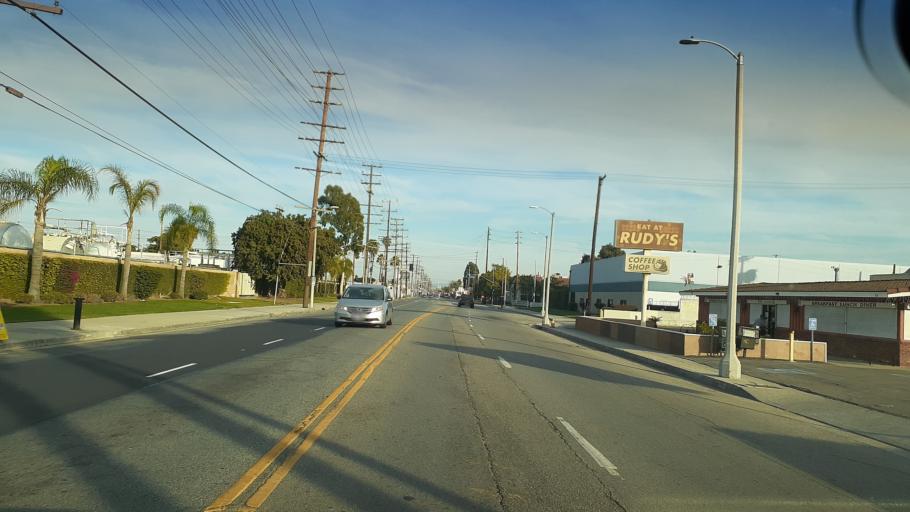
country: US
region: California
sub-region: Los Angeles County
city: West Carson
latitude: 33.7803
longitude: -118.2567
